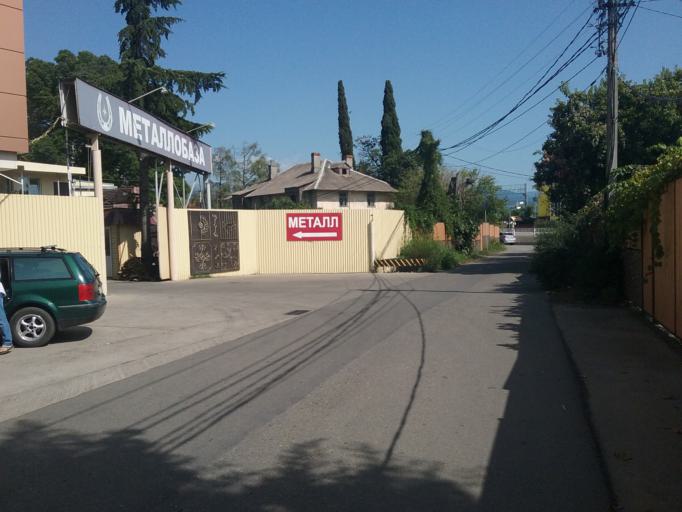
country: RU
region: Krasnodarskiy
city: Vysokoye
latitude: 43.3990
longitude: 39.9951
